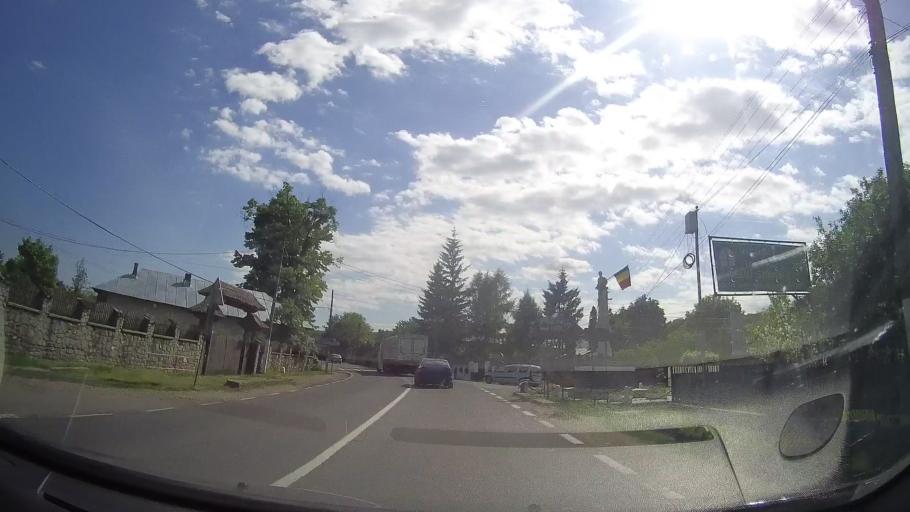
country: RO
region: Prahova
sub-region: Comuna Izvoarele
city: Homoraciu
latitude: 45.2693
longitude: 26.0154
